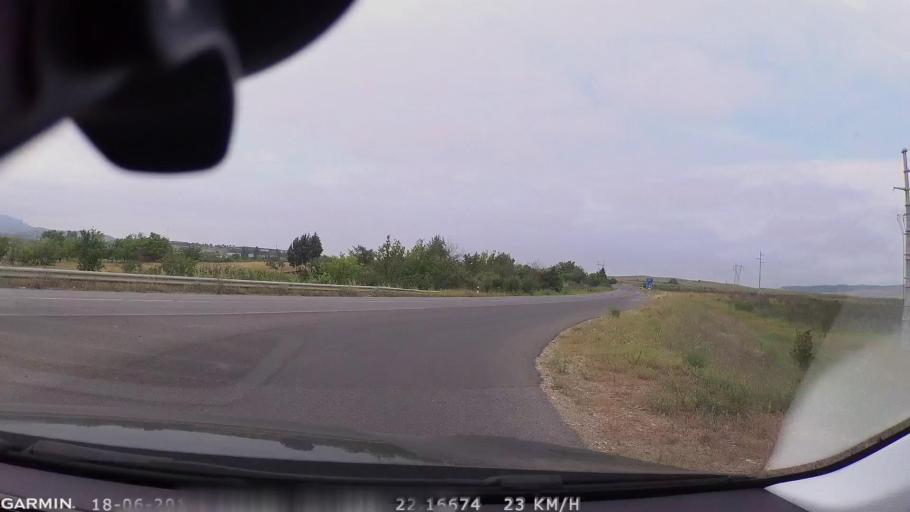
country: MK
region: Stip
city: Shtip
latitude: 41.7686
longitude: 22.1665
